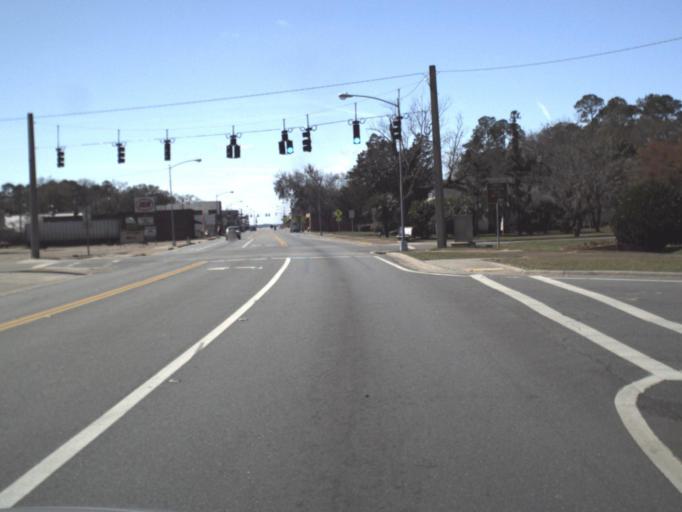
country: US
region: Florida
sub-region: Gadsden County
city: Chattahoochee
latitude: 30.7050
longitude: -84.8428
